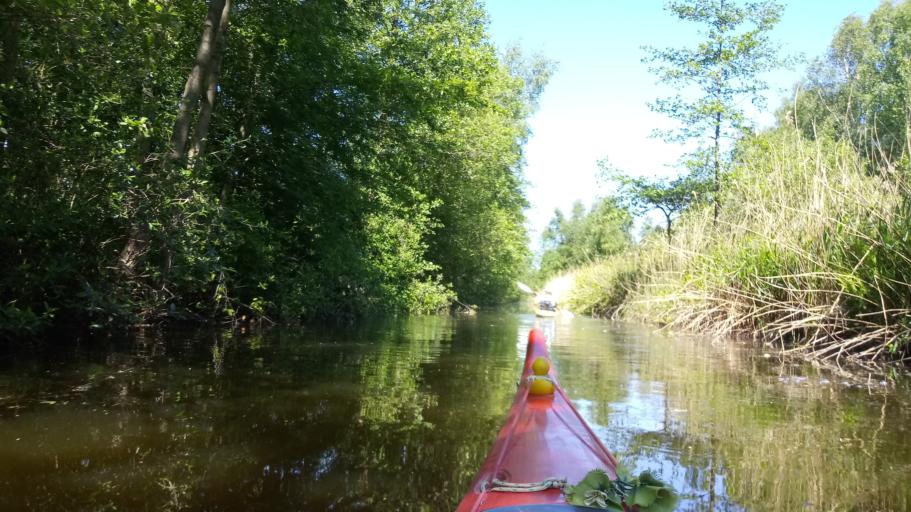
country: NL
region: South Holland
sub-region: Gemeente Nieuwkoop
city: Nieuwkoop
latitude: 52.1584
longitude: 4.8181
